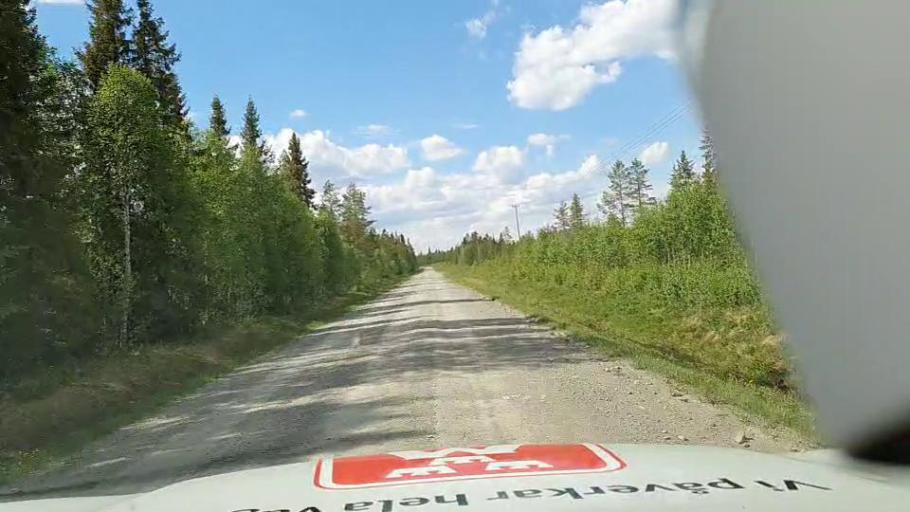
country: SE
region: Vaesterbotten
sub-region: Vilhelmina Kommun
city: Sjoberg
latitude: 64.5426
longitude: 15.6536
